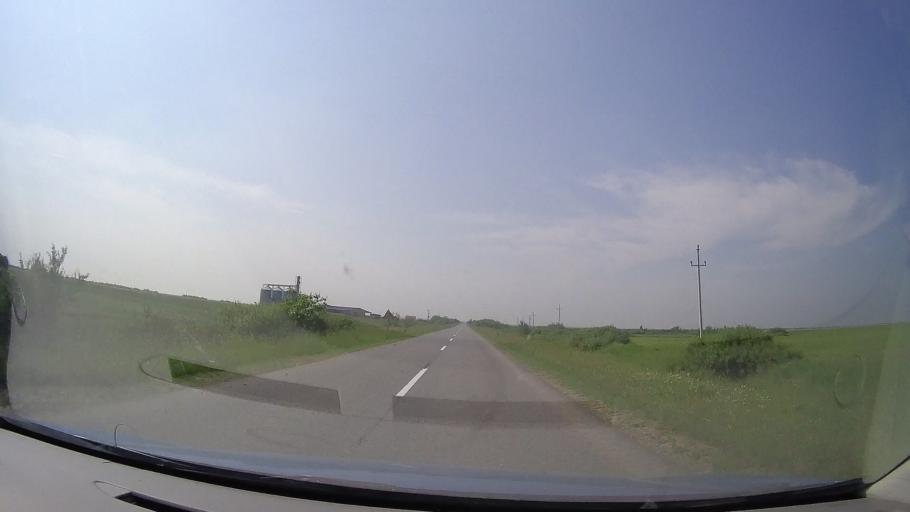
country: RS
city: Jarkovac
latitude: 45.2564
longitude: 20.7637
